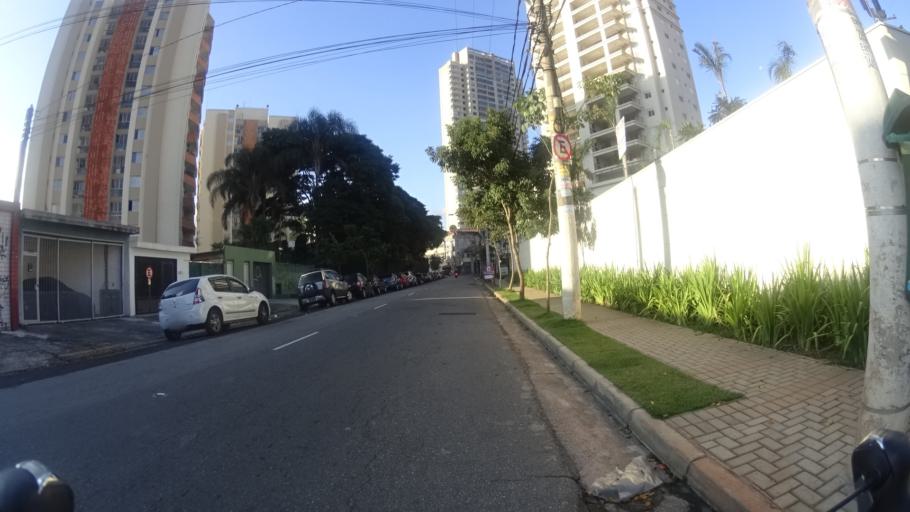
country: BR
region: Sao Paulo
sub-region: Sao Paulo
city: Sao Paulo
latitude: -23.4982
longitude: -46.6317
